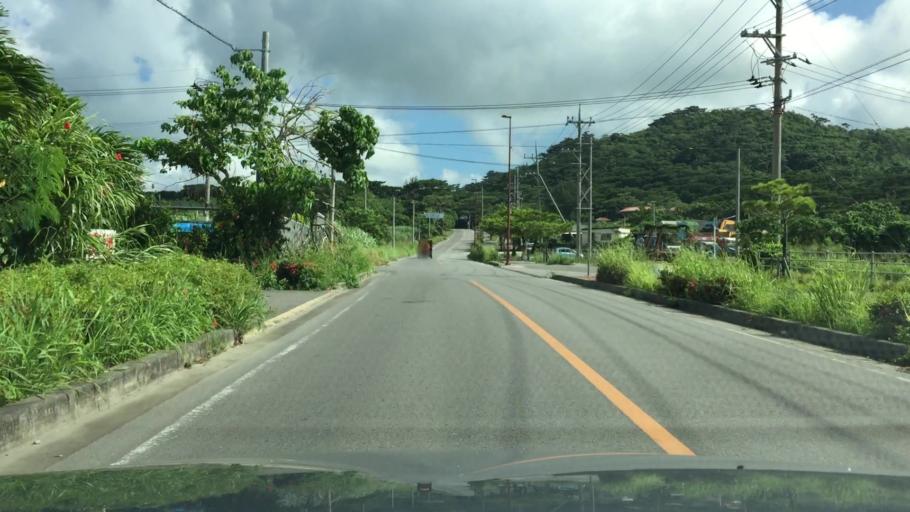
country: JP
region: Okinawa
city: Ishigaki
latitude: 24.3649
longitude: 124.1571
